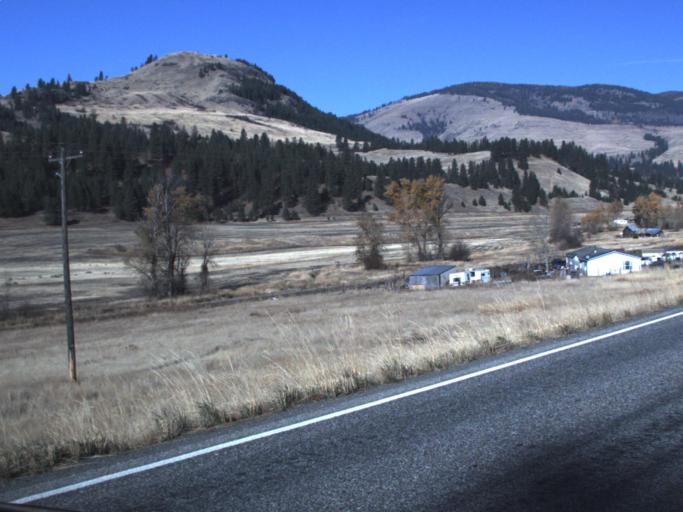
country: CA
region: British Columbia
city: Grand Forks
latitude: 48.8596
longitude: -118.6046
